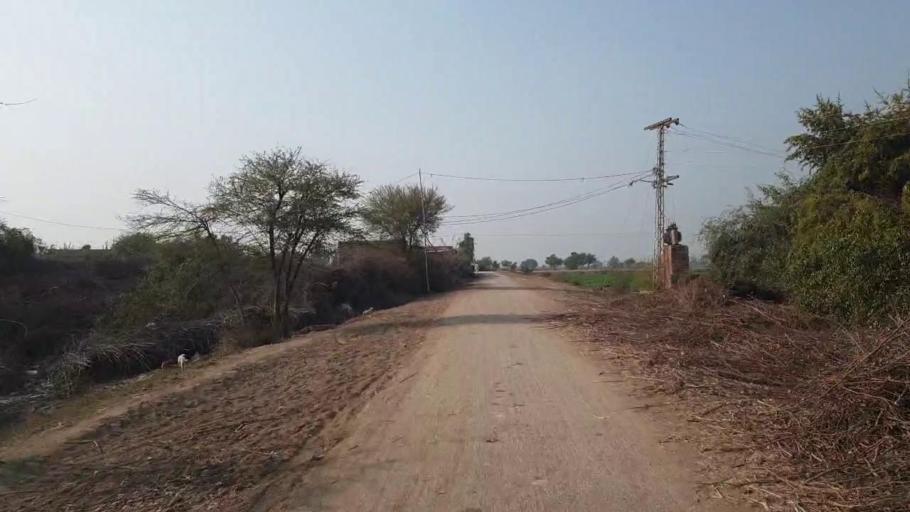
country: PK
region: Sindh
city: Bhit Shah
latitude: 25.9002
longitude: 68.4719
